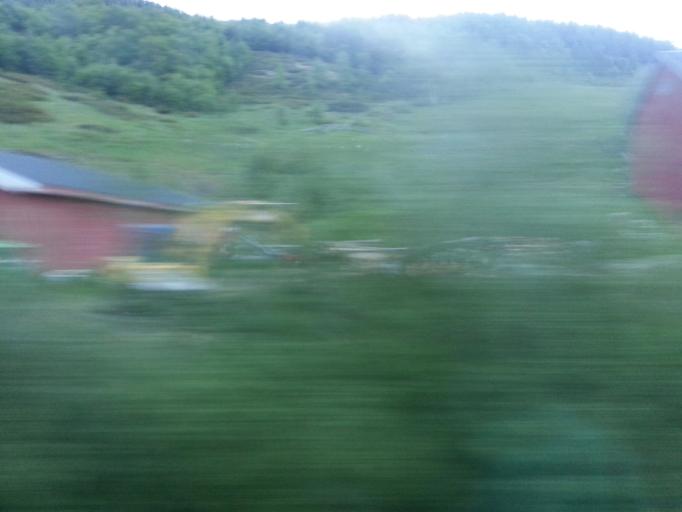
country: NO
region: Oppland
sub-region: Dovre
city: Dombas
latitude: 62.0529
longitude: 9.1421
